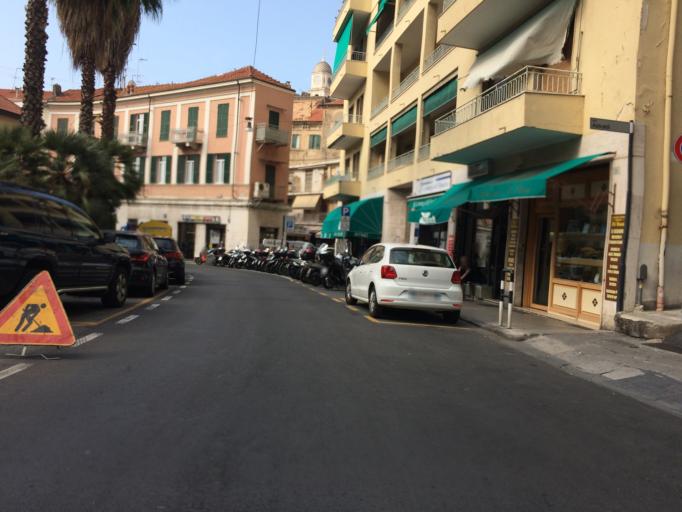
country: IT
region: Liguria
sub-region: Provincia di Imperia
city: San Remo
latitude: 43.8191
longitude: 7.7771
